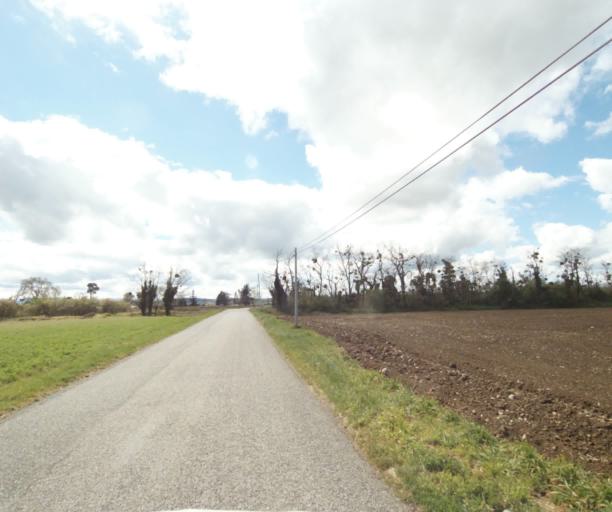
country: FR
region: Midi-Pyrenees
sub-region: Departement de l'Ariege
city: Saverdun
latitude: 43.2531
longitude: 1.5979
